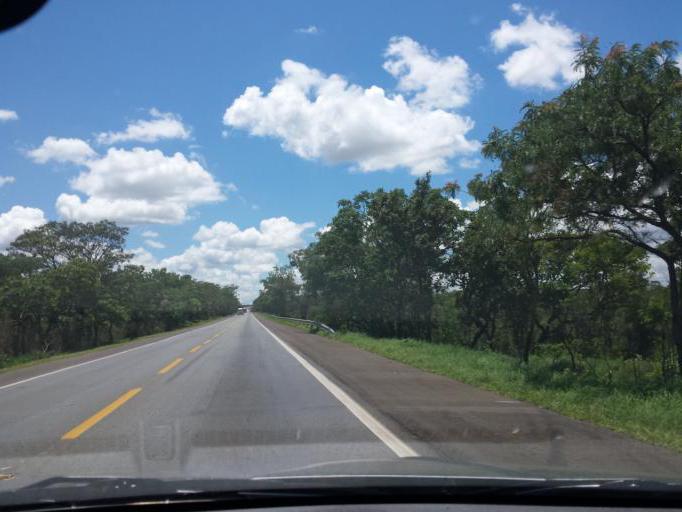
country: BR
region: Goias
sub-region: Cristalina
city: Cristalina
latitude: -16.6535
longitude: -47.7330
